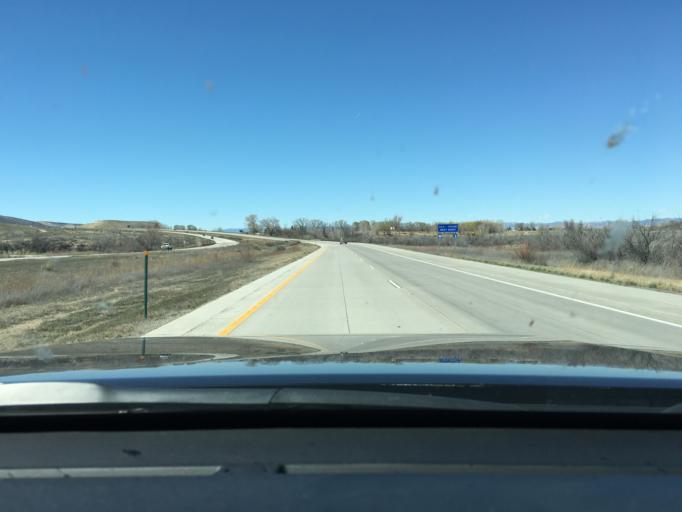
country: US
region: Colorado
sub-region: Mesa County
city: Loma
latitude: 39.1735
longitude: -108.7978
